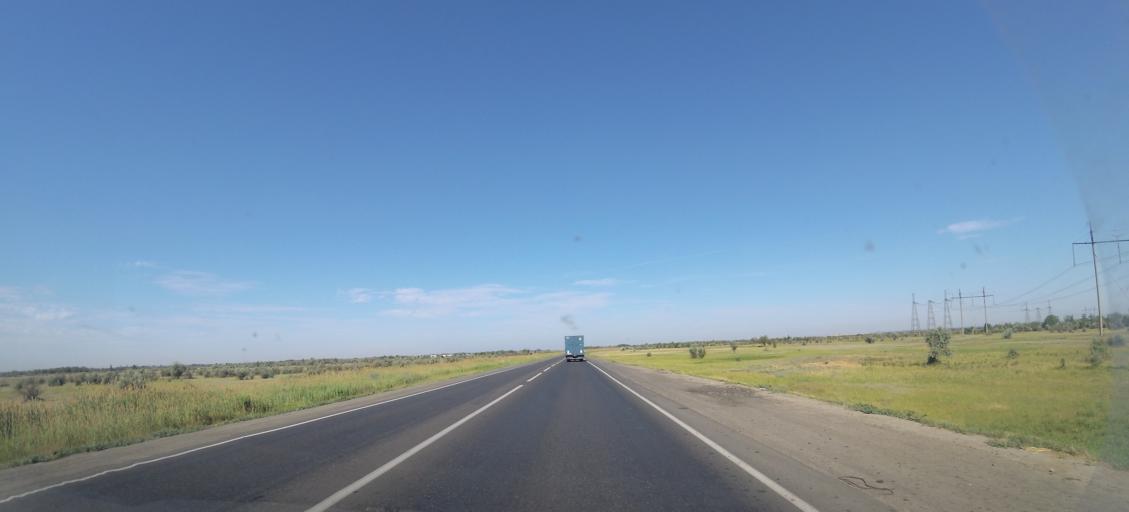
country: RU
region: Volgograd
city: Novyy Rogachik
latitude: 48.6805
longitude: 44.0360
